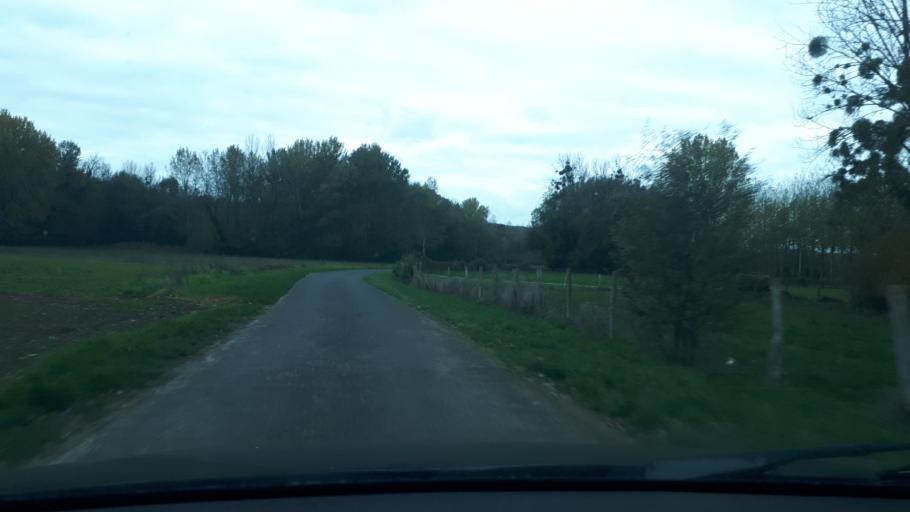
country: FR
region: Centre
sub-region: Departement du Loir-et-Cher
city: Villiers-sur-Loir
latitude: 47.7771
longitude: 0.9594
